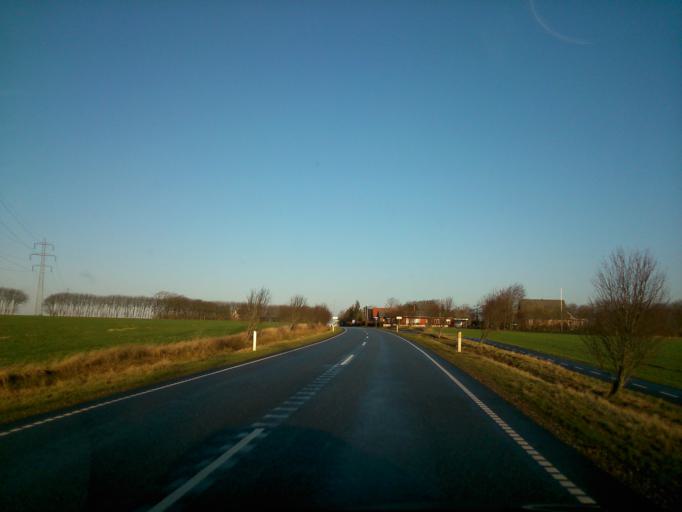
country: DK
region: Central Jutland
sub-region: Ringkobing-Skjern Kommune
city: Tarm
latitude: 55.9817
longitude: 8.5905
